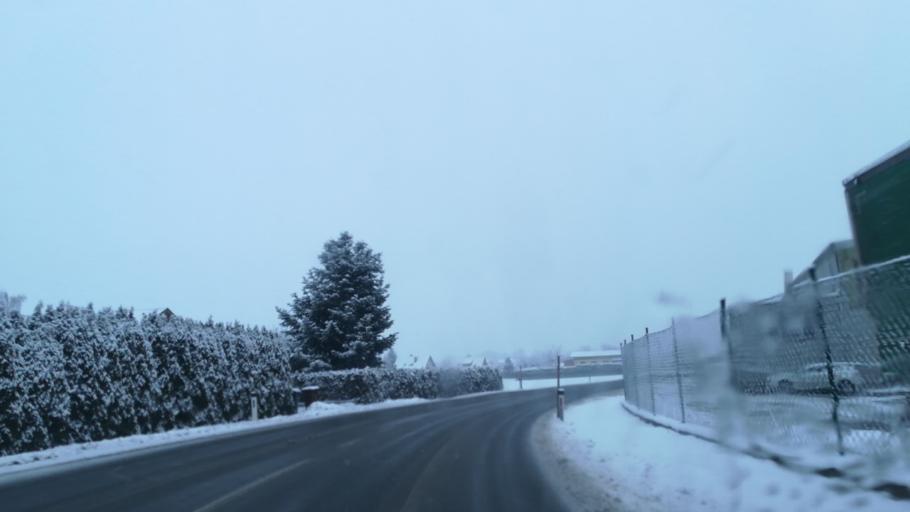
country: AT
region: Styria
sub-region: Politischer Bezirk Murtal
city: Knittelfeld
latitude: 47.2186
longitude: 14.8119
